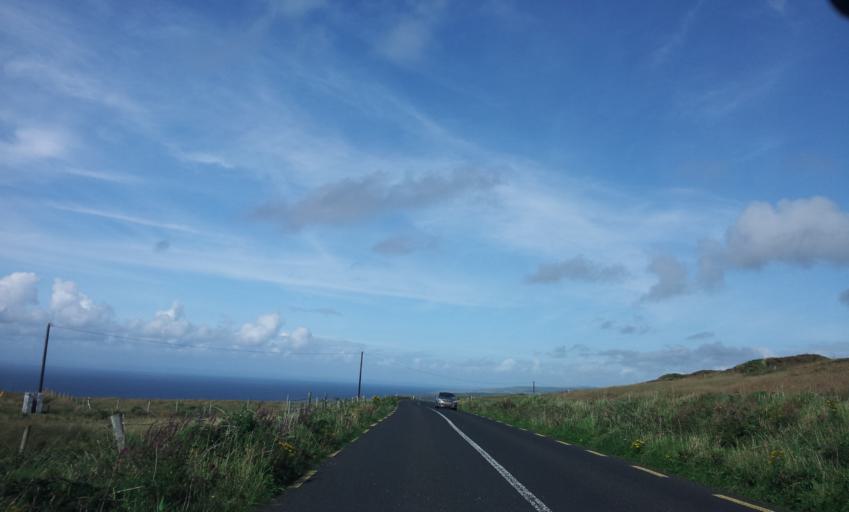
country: IE
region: Munster
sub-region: An Clar
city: Kilrush
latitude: 52.9822
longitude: -9.4187
